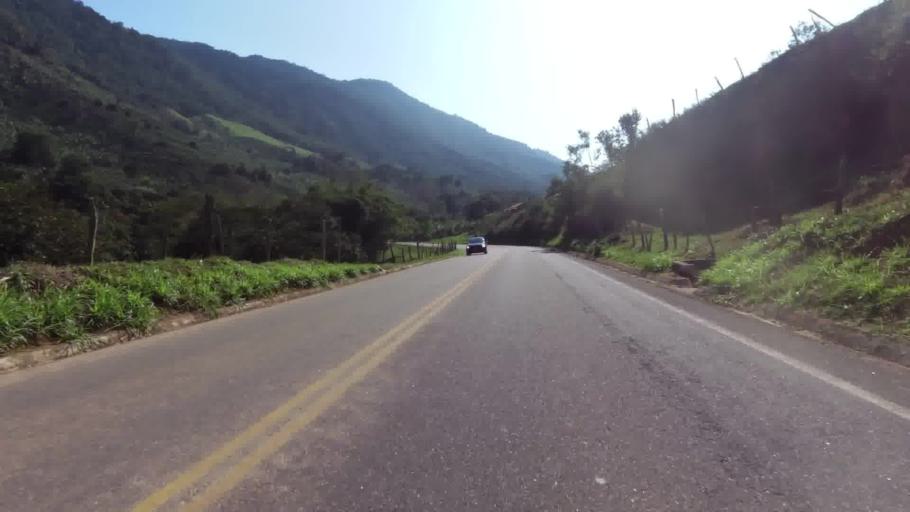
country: BR
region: Espirito Santo
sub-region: Alfredo Chaves
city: Alfredo Chaves
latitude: -20.6165
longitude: -40.7784
